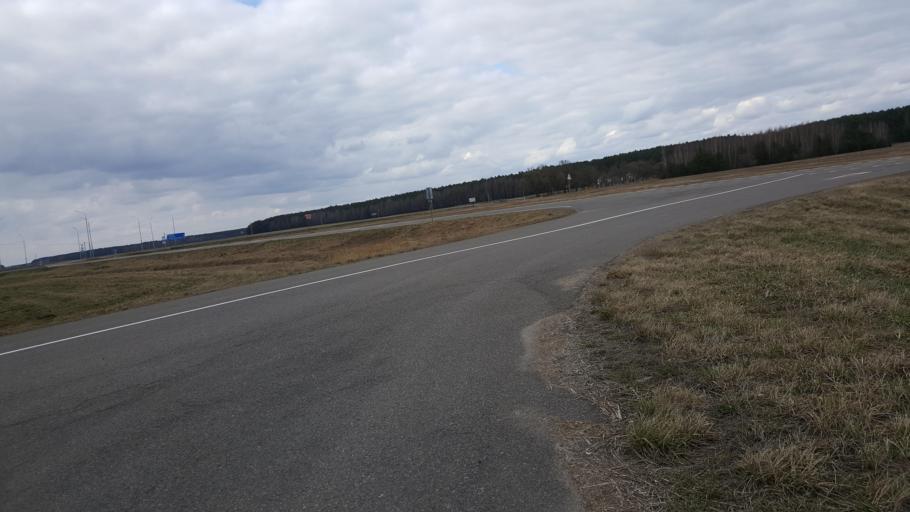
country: BY
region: Brest
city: Kamyanyuki
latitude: 52.4936
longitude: 23.7837
